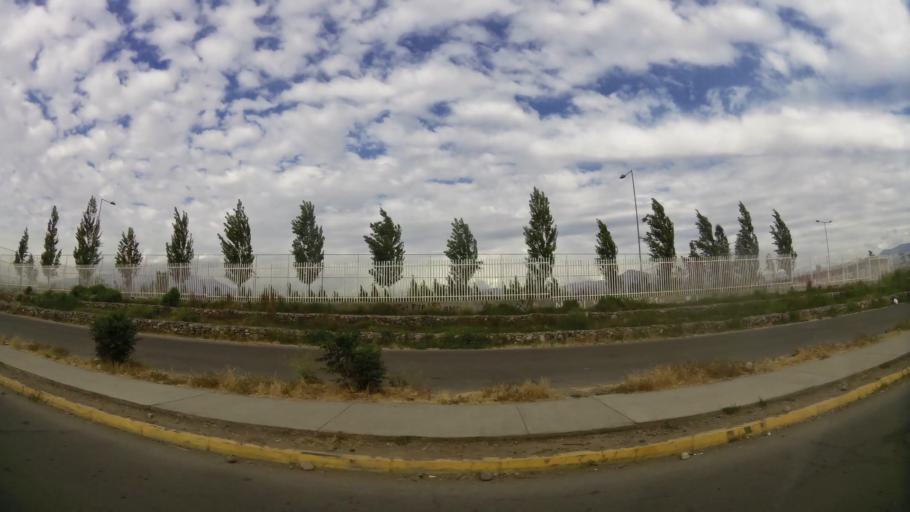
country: CL
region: Santiago Metropolitan
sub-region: Provincia de Cordillera
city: Puente Alto
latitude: -33.6253
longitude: -70.6177
